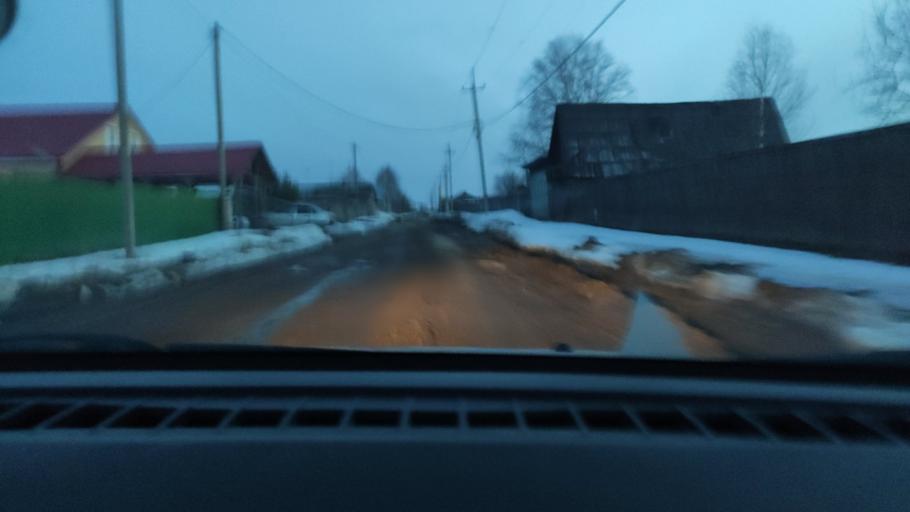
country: RU
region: Perm
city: Yug
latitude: 57.7318
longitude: 56.1683
